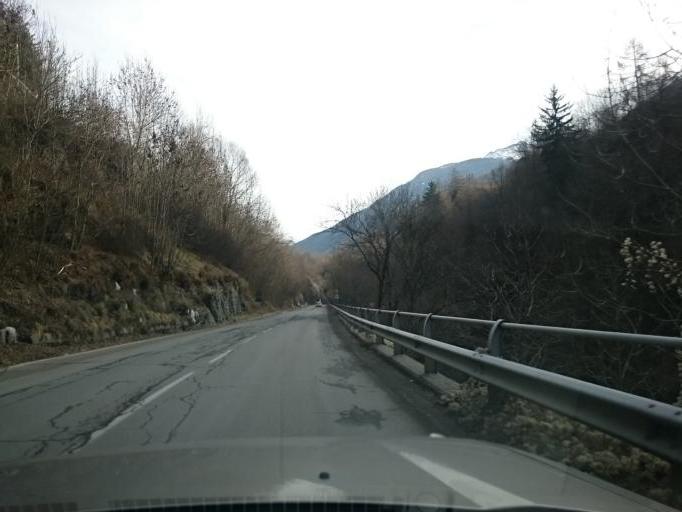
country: IT
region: Lombardy
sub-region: Provincia di Brescia
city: Corteno Golgi
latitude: 46.1664
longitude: 10.2274
